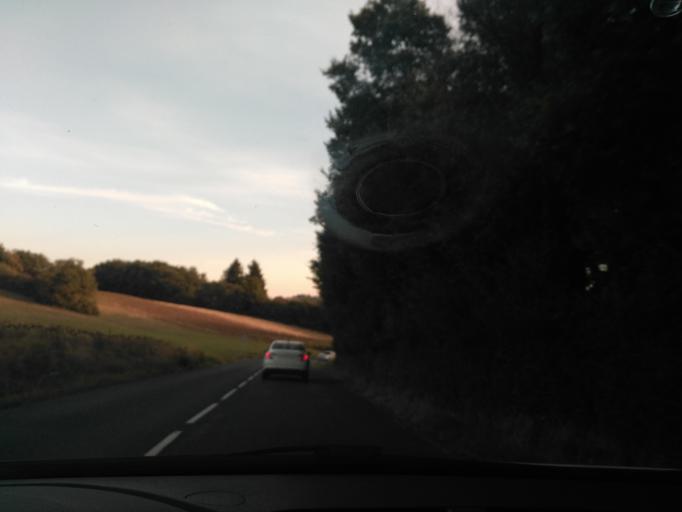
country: FR
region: Rhone-Alpes
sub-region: Departement du Rhone
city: Limonest
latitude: 45.8430
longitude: 4.7933
